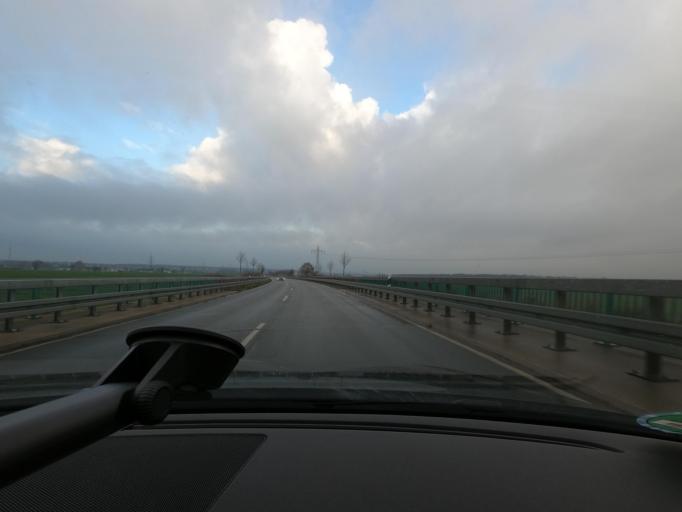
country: DE
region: North Rhine-Westphalia
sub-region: Regierungsbezirk Detmold
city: Buren
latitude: 51.5776
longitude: 8.5406
